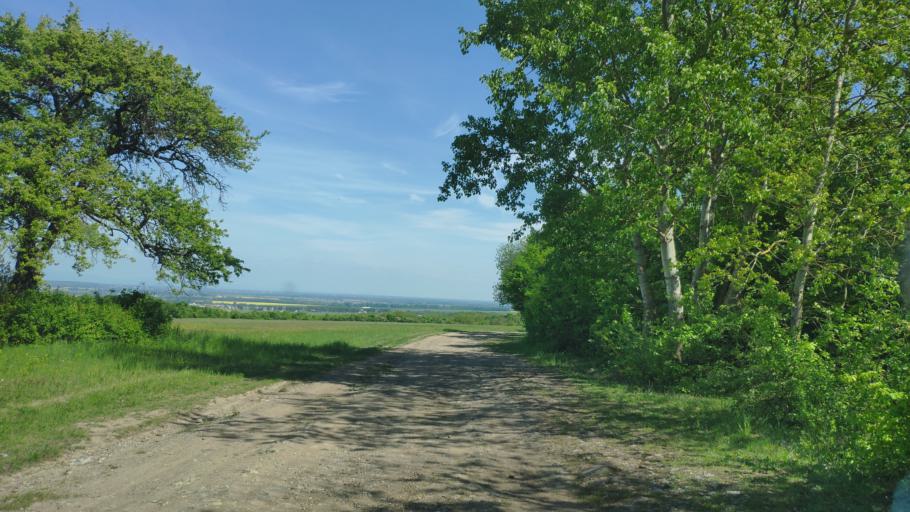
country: SK
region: Kosicky
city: Secovce
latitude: 48.6994
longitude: 21.5929
